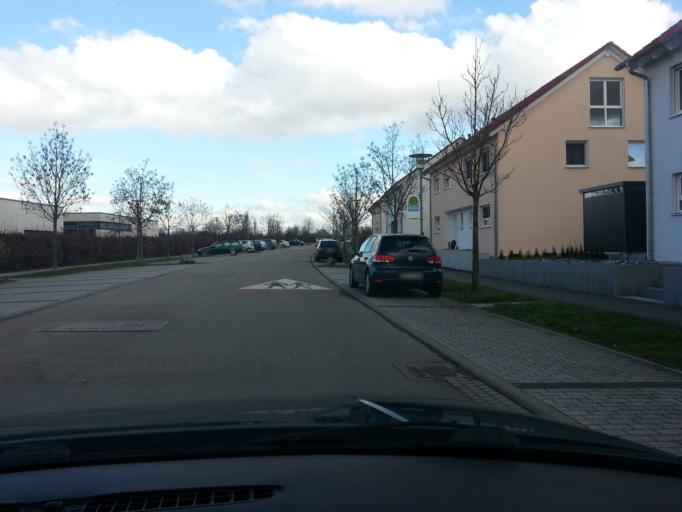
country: DE
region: Baden-Wuerttemberg
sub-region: Regierungsbezirk Stuttgart
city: Oedheim
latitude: 49.2120
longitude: 9.2572
